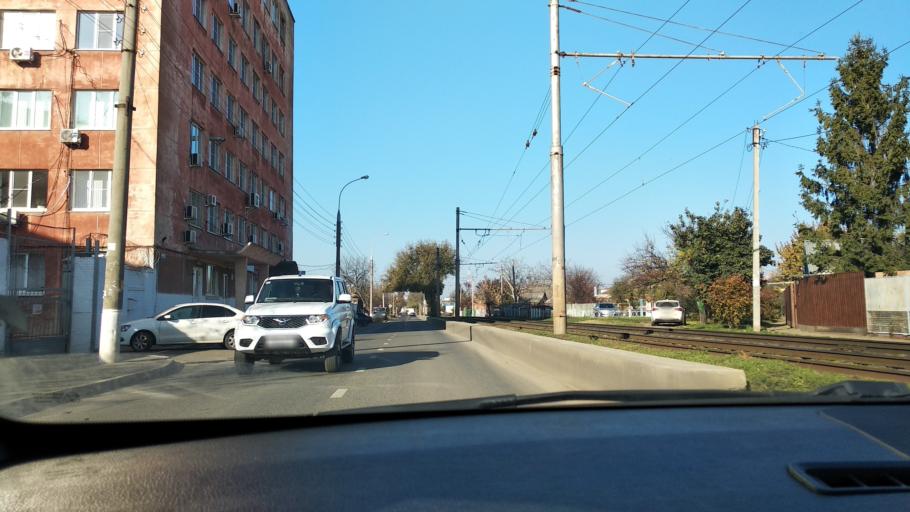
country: RU
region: Krasnodarskiy
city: Krasnodar
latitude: 45.0081
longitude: 39.0153
